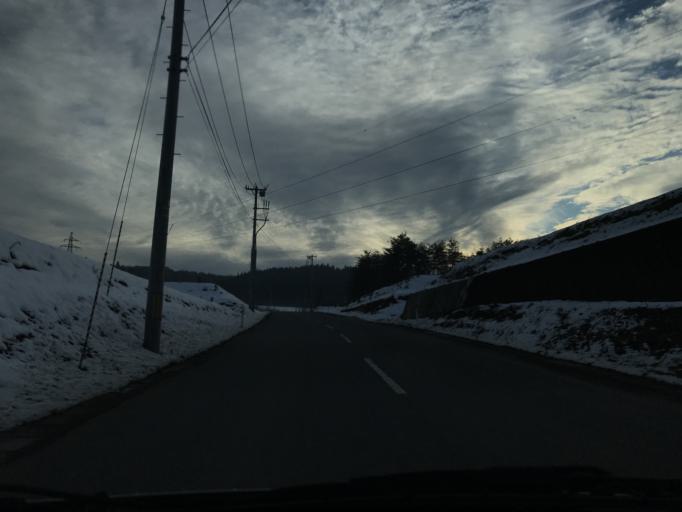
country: JP
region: Iwate
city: Mizusawa
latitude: 39.0544
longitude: 141.0827
